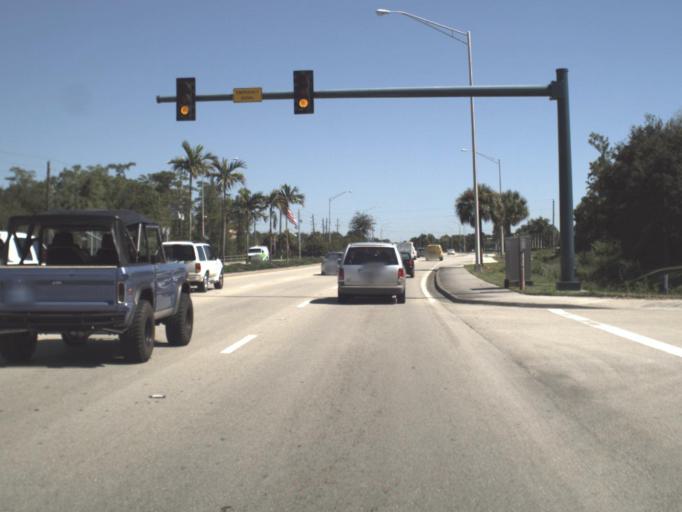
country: US
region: Florida
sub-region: Collier County
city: Vineyards
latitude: 26.2116
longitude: -81.7493
